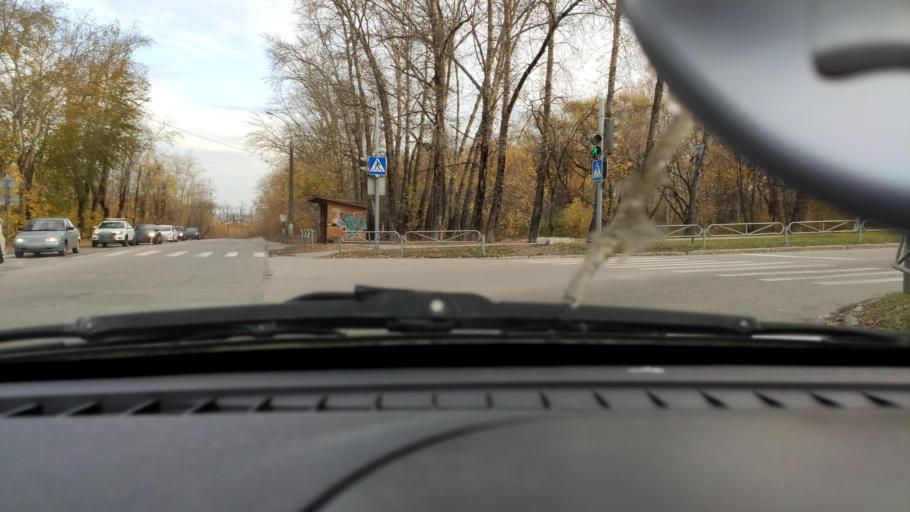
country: RU
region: Perm
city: Perm
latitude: 58.1274
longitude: 56.3725
